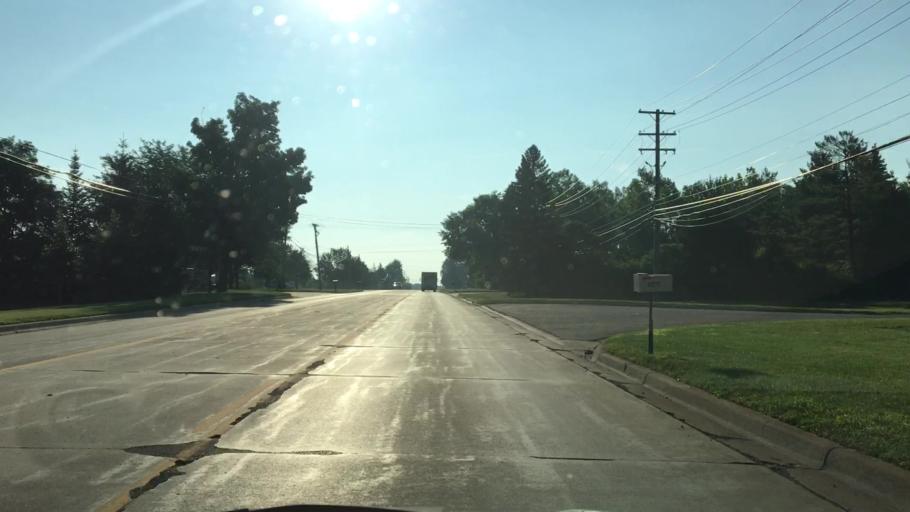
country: US
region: Michigan
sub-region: Oakland County
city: Wixom
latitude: 42.5085
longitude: -83.5256
